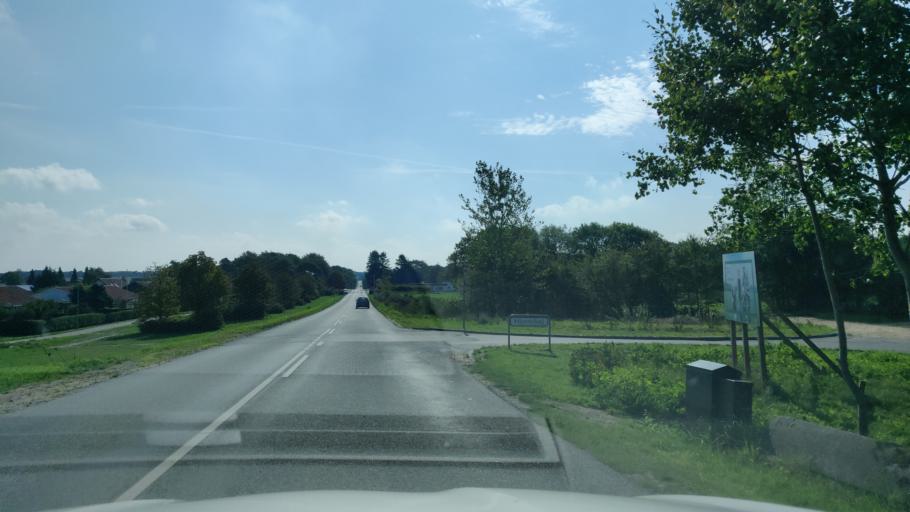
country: DK
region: Central Jutland
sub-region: Herning Kommune
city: Avlum
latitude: 56.2164
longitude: 8.8472
